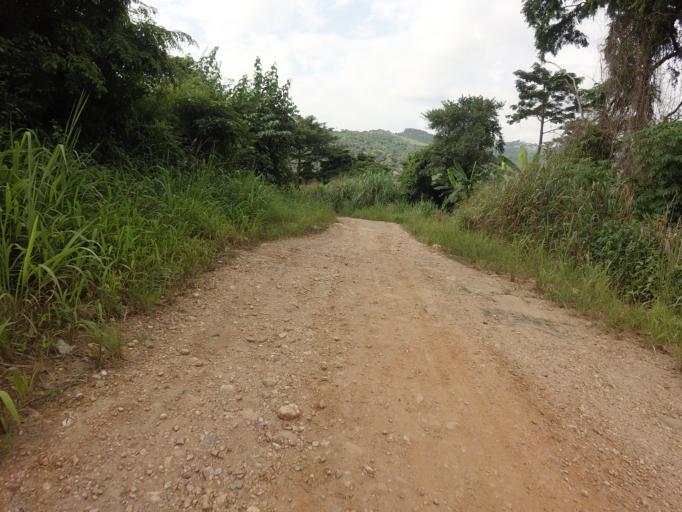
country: GH
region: Volta
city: Kpandu
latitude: 6.8747
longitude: 0.4410
